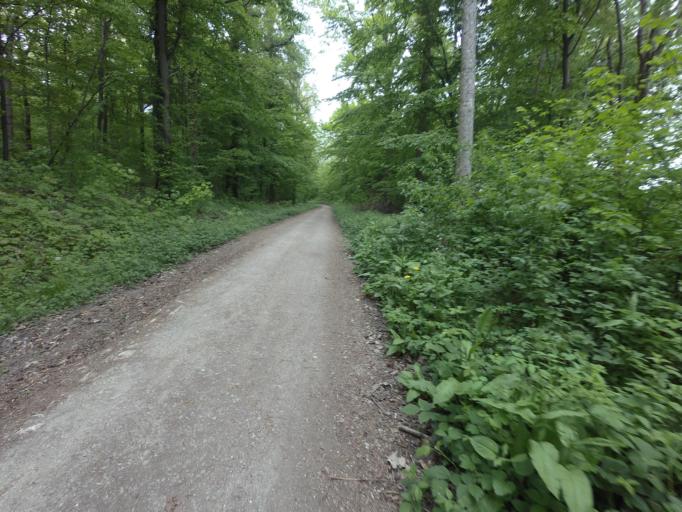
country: DE
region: Lower Saxony
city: Diekholzen
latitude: 52.1329
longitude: 9.9054
